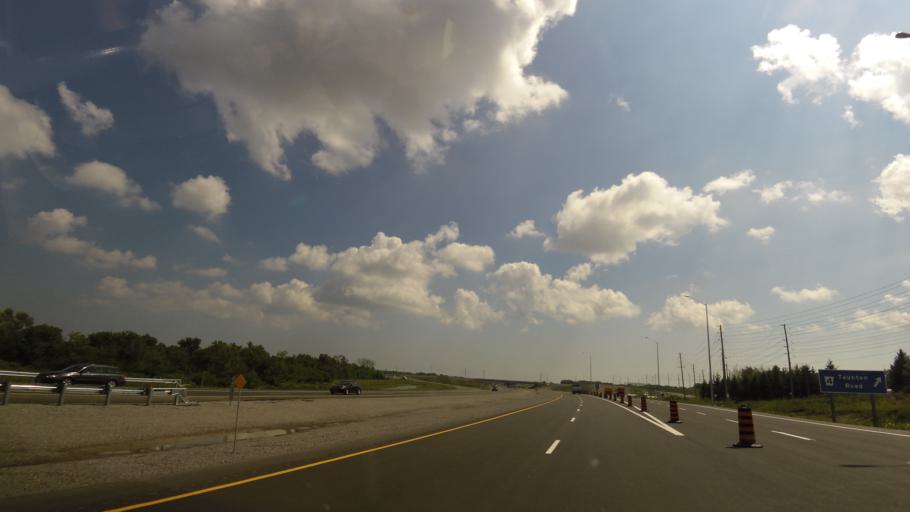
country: CA
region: Ontario
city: Ajax
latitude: 43.9119
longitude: -78.9980
